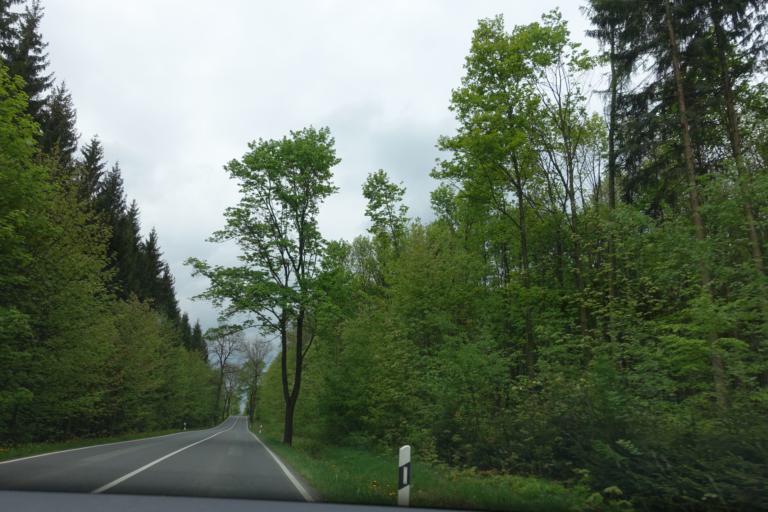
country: DE
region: Saxony
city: Bornichen
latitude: 50.7349
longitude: 13.1335
